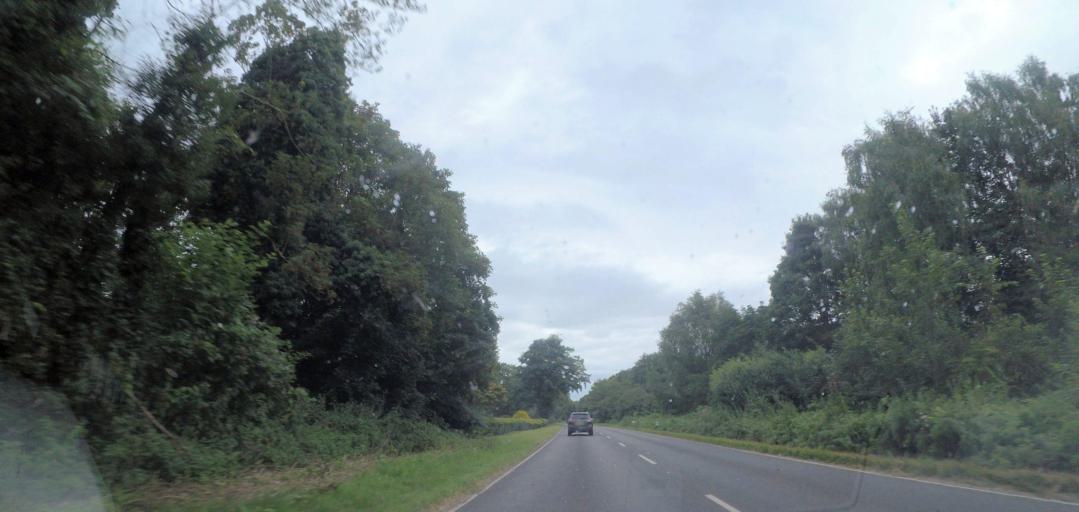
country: GB
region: England
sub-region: Norfolk
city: Spixworth
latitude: 52.6928
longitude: 1.3371
